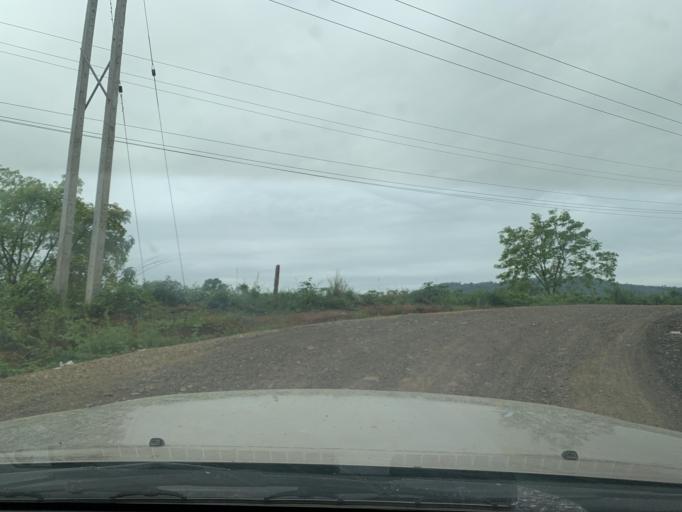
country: TH
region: Nan
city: Mae Charim
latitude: 18.4167
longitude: 101.4546
